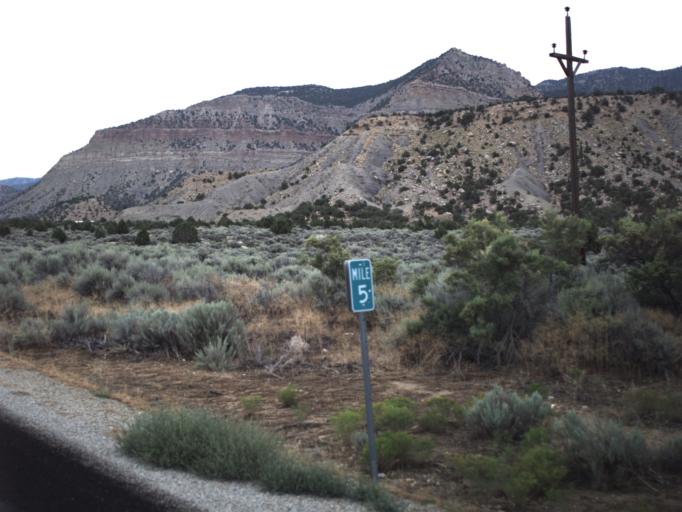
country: US
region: Utah
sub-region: Carbon County
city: East Carbon City
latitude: 39.5119
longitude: -110.3939
